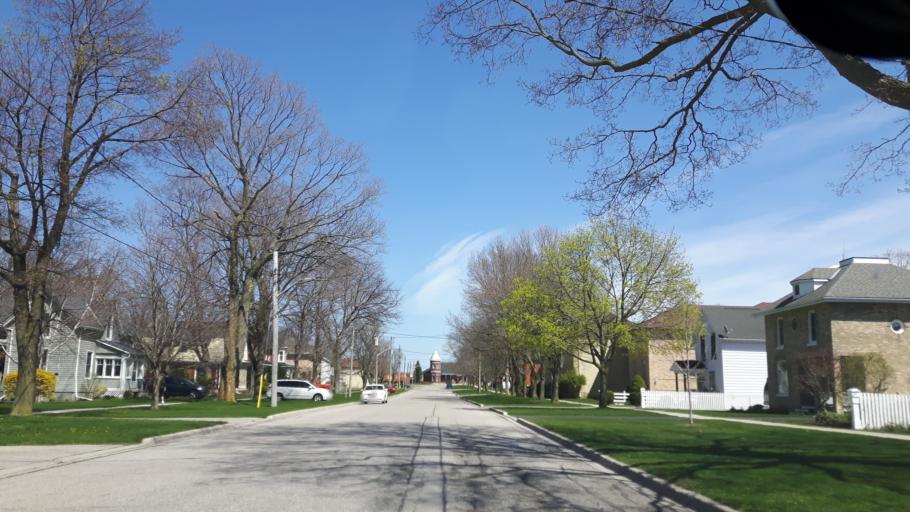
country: CA
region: Ontario
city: Goderich
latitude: 43.7431
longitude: -81.7038
